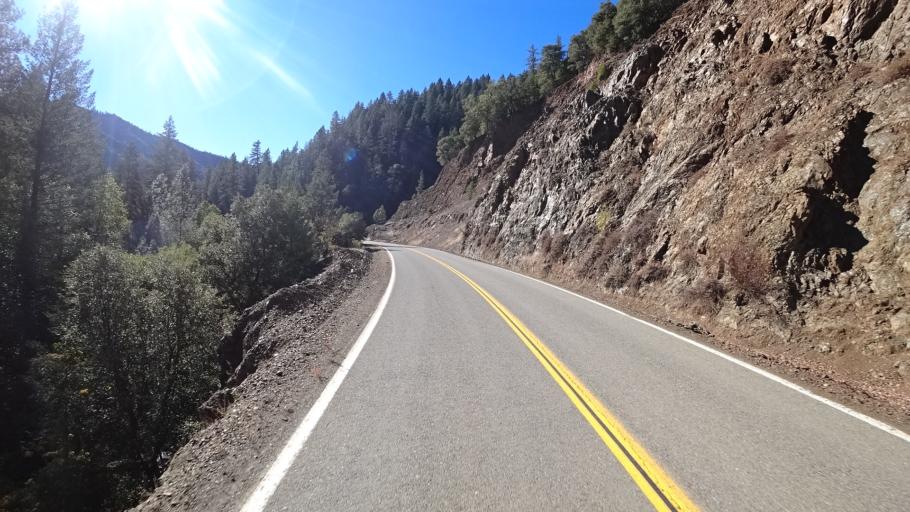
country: US
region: California
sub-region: Trinity County
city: Weaverville
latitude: 41.1707
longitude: -123.0958
